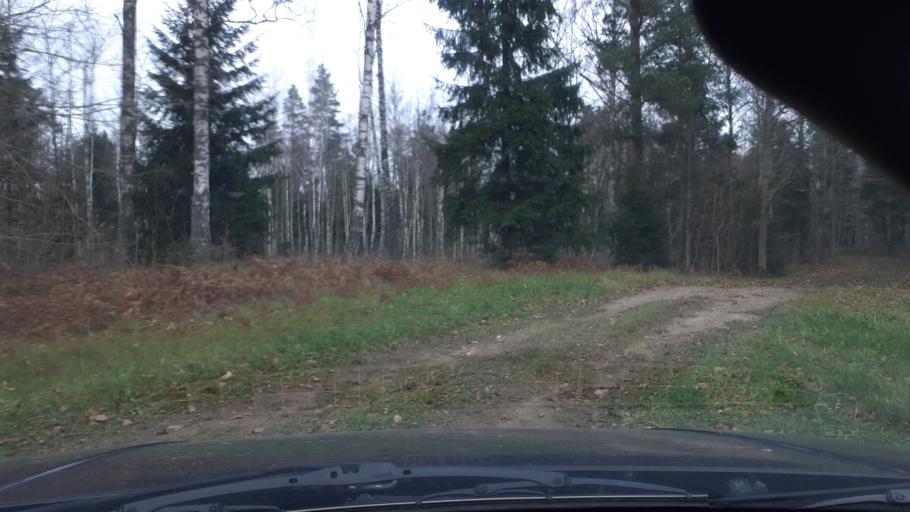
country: LV
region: Alsunga
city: Alsunga
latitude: 56.9418
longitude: 21.6452
